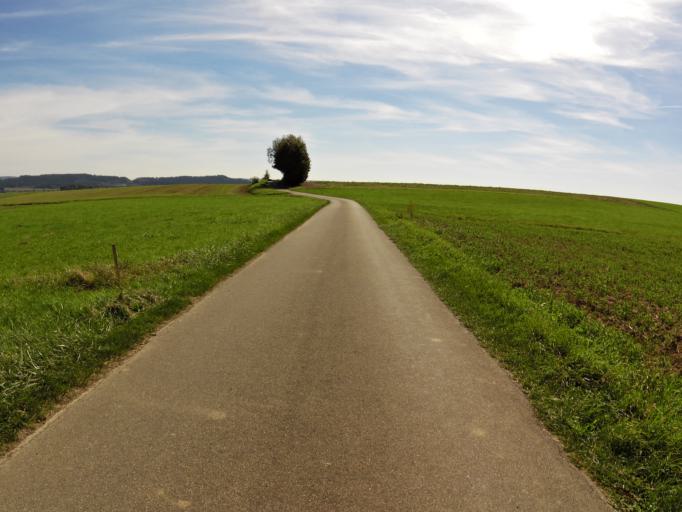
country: DE
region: Baden-Wuerttemberg
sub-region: Freiburg Region
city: Bad Durrheim
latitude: 48.0127
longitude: 8.4982
